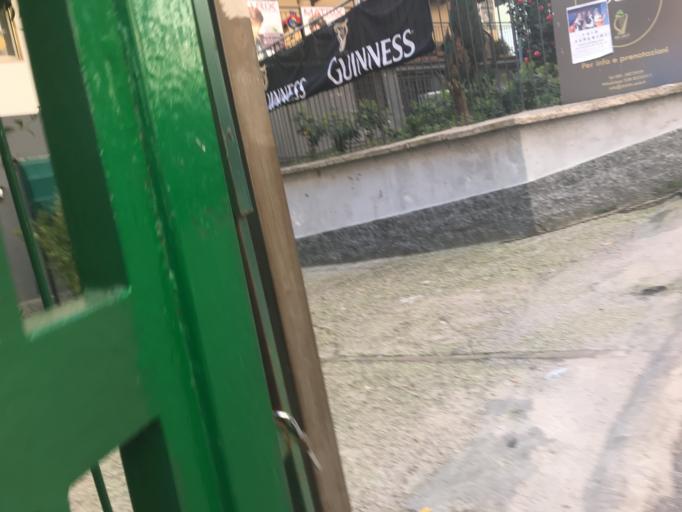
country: IT
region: Campania
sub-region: Provincia di Napoli
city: Napoli
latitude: 40.8609
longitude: 14.2213
